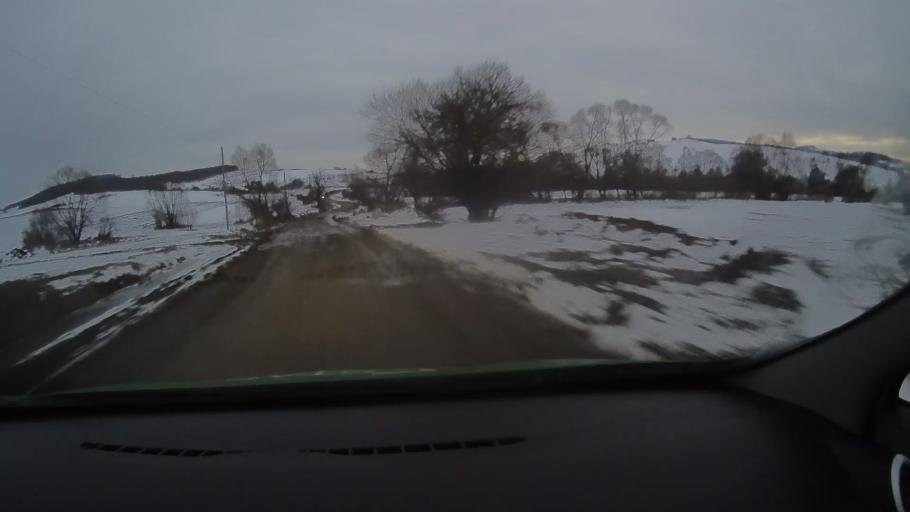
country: RO
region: Harghita
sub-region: Comuna Darjiu
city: Darjiu
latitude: 46.2087
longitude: 25.2424
